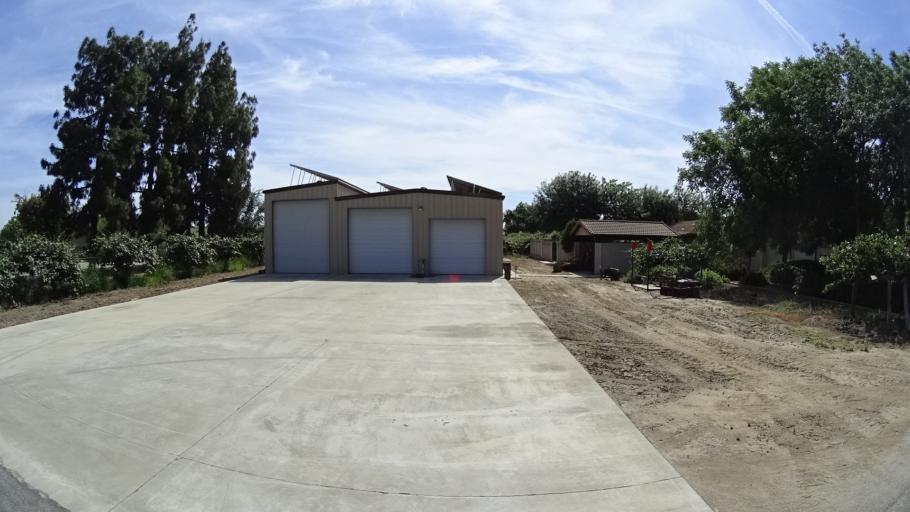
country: US
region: California
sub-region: Kings County
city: Hanford
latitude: 36.3578
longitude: -119.6297
